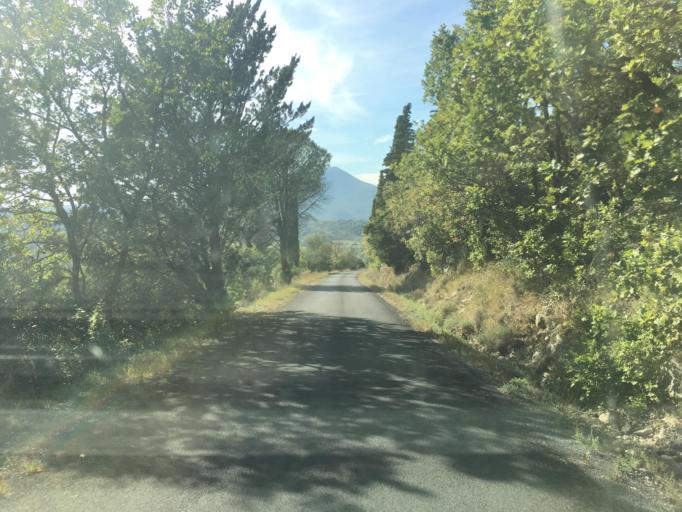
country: FR
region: Languedoc-Roussillon
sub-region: Departement de l'Herault
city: Saint-Bauzille-de-Putois
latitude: 43.9060
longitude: 3.7432
